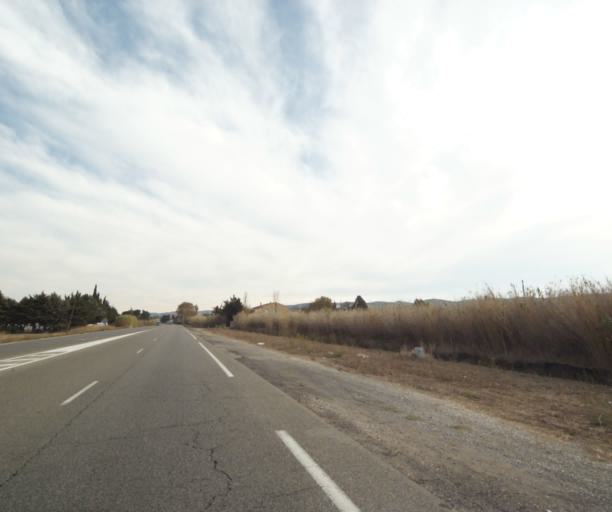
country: FR
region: Provence-Alpes-Cote d'Azur
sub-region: Departement des Bouches-du-Rhone
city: Gignac-la-Nerthe
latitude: 43.3947
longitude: 5.2223
